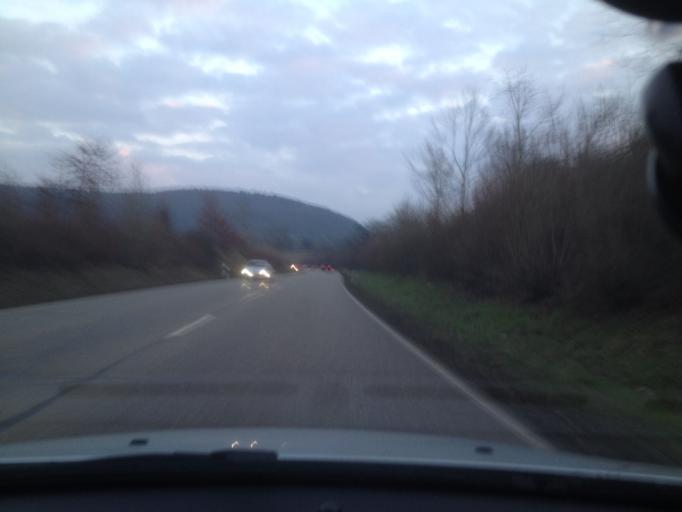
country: DE
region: Baden-Wuerttemberg
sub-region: Karlsruhe Region
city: Ettlingen
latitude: 48.9574
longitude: 8.4098
